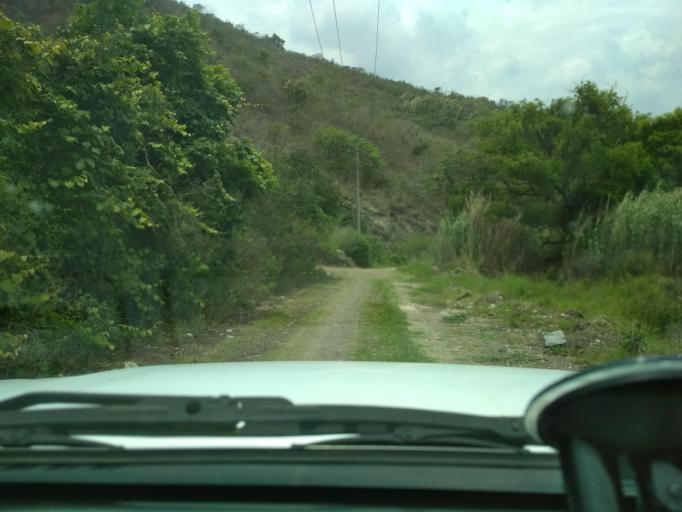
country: MX
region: Veracruz
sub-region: Nogales
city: Taza de Agua Ojo Zarco
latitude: 18.7727
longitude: -97.2100
